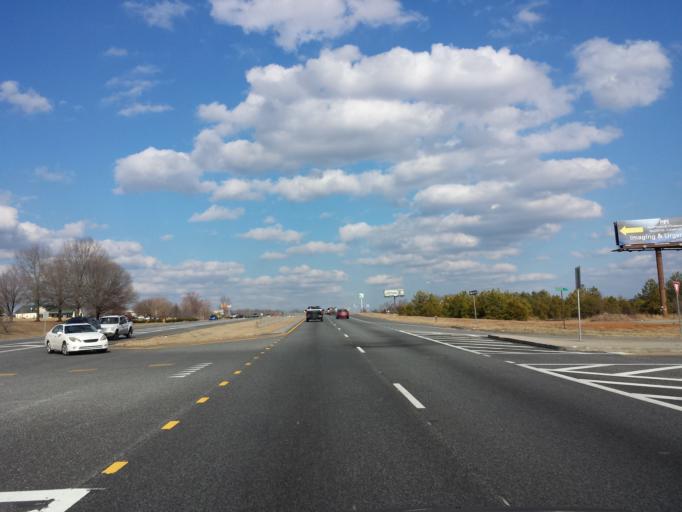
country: US
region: Georgia
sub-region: Dawson County
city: Dawsonville
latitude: 34.3599
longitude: -84.0416
